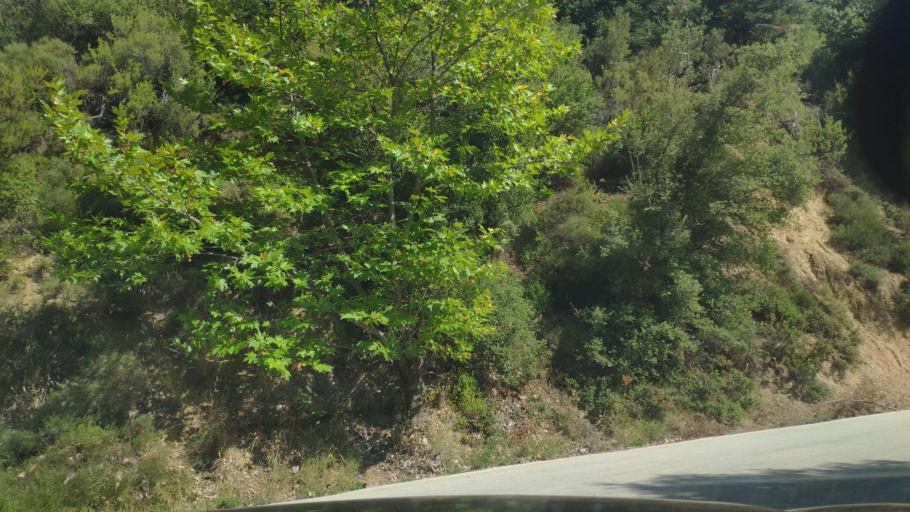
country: GR
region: Peloponnese
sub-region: Nomos Korinthias
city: Nemea
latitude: 37.8590
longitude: 22.3822
